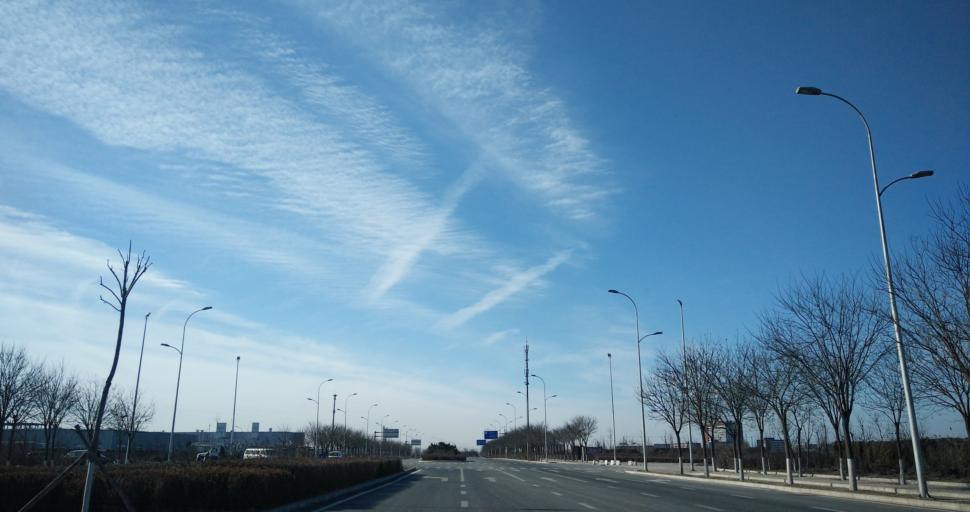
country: CN
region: Beijing
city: Qingyundian
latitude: 39.7240
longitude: 116.5137
